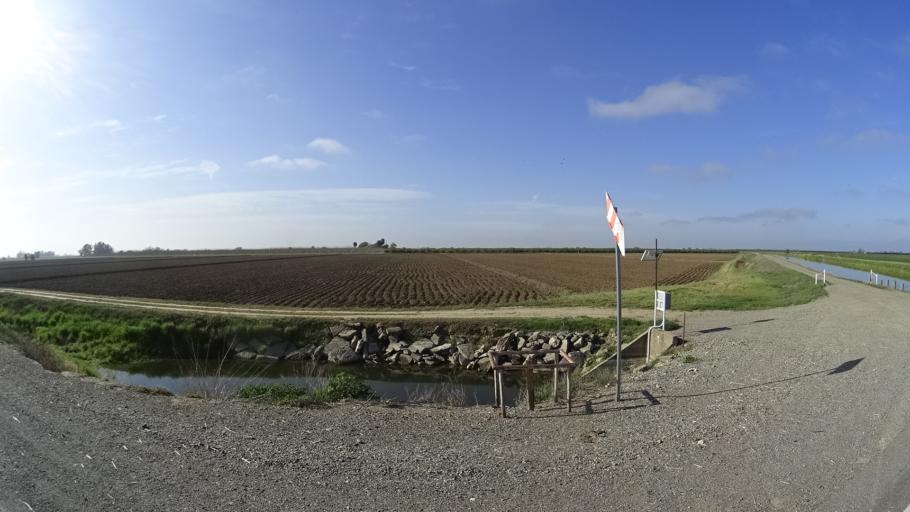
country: US
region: California
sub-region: Glenn County
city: Willows
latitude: 39.5822
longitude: -122.1221
